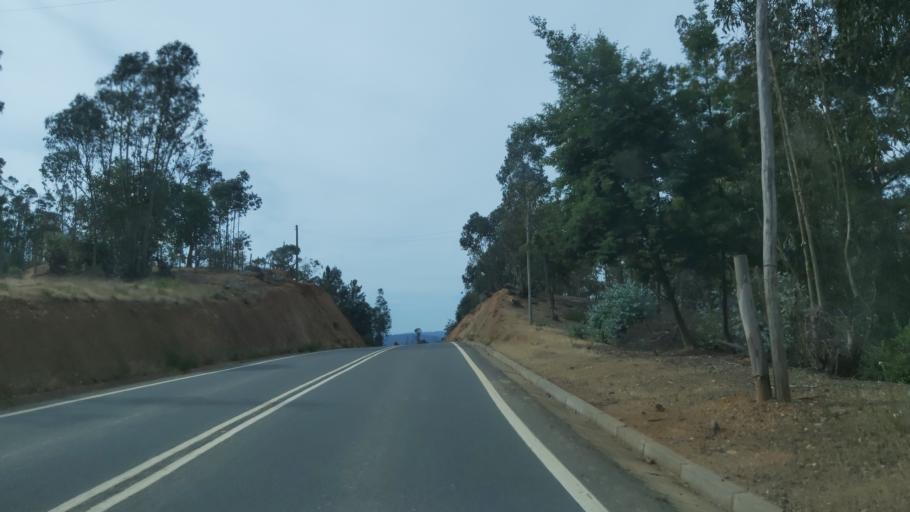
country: CL
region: Maule
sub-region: Provincia de Talca
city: Constitucion
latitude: -34.9185
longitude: -71.9922
